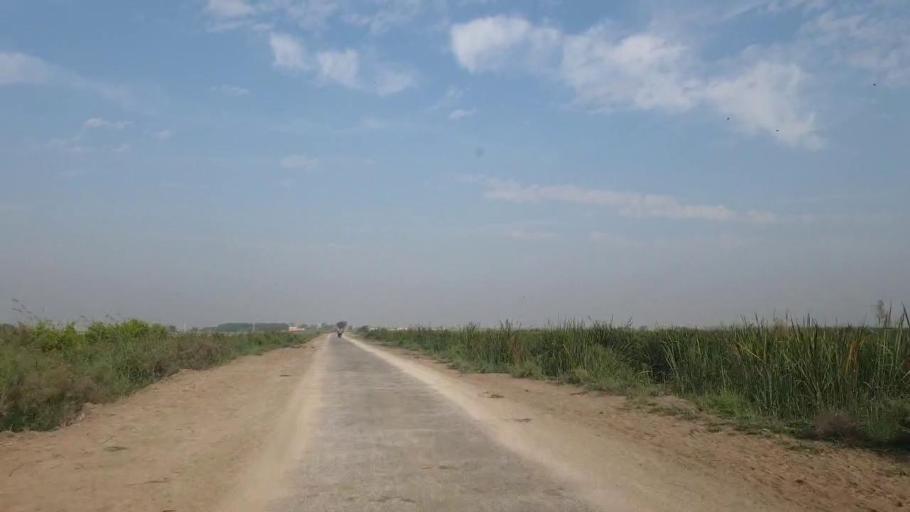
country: PK
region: Sindh
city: Tando Bago
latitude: 24.8510
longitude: 68.9711
